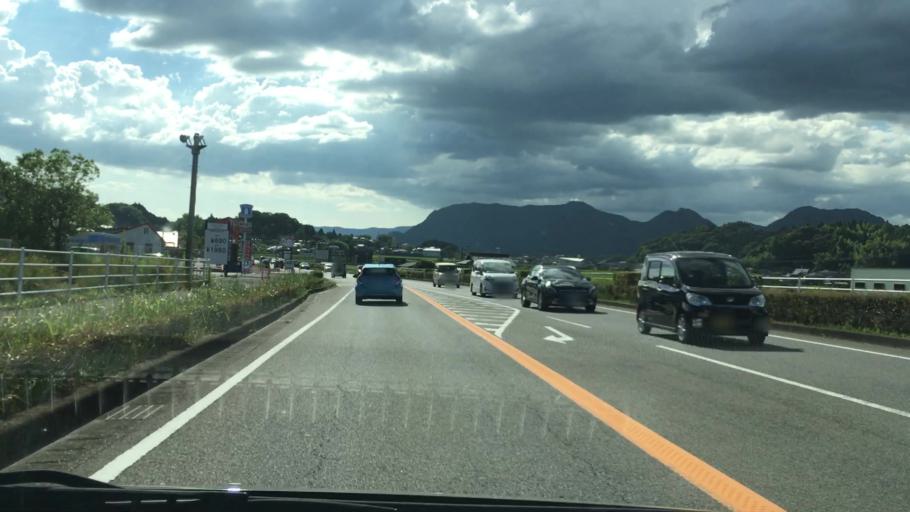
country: JP
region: Saga Prefecture
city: Takeocho-takeo
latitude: 33.1925
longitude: 129.9604
